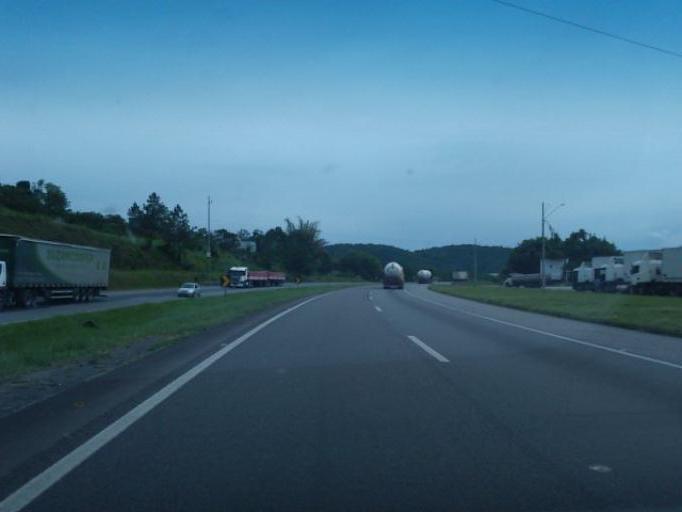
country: BR
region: Sao Paulo
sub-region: Jacupiranga
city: Jacupiranga
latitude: -24.6772
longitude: -47.9805
